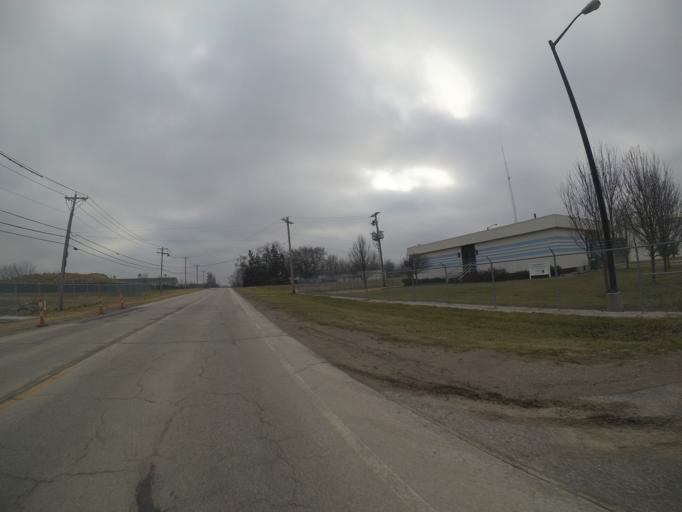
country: US
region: Ohio
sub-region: Wood County
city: Walbridge
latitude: 41.6142
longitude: -83.5125
